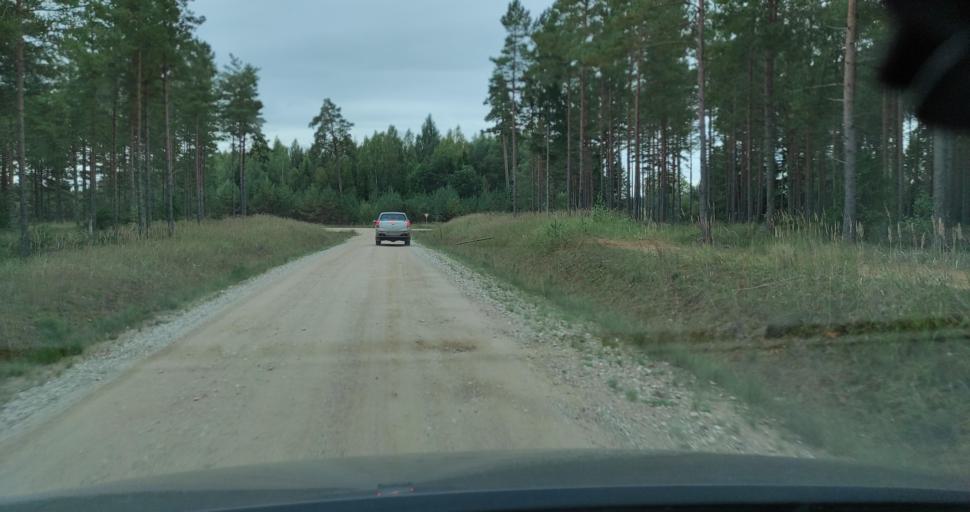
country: LV
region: Kuldigas Rajons
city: Kuldiga
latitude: 57.0820
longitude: 22.2318
